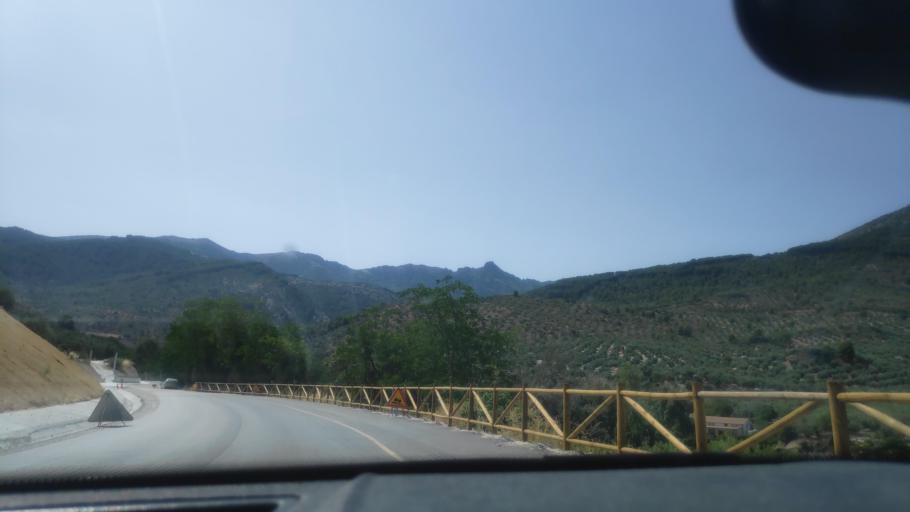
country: ES
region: Andalusia
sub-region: Provincia de Jaen
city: Jodar
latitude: 37.8016
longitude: -3.4133
